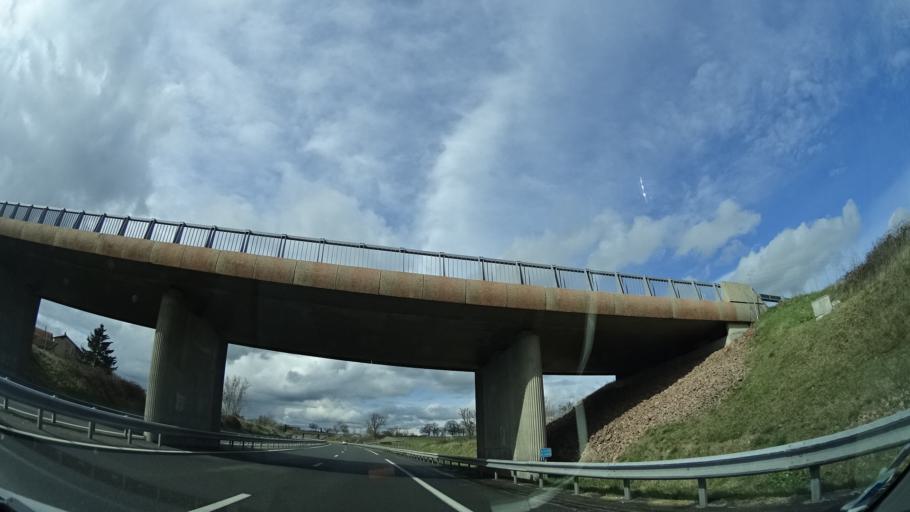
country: FR
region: Rhone-Alpes
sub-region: Departement de la Loire
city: La Pacaudiere
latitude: 46.1780
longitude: 3.8791
